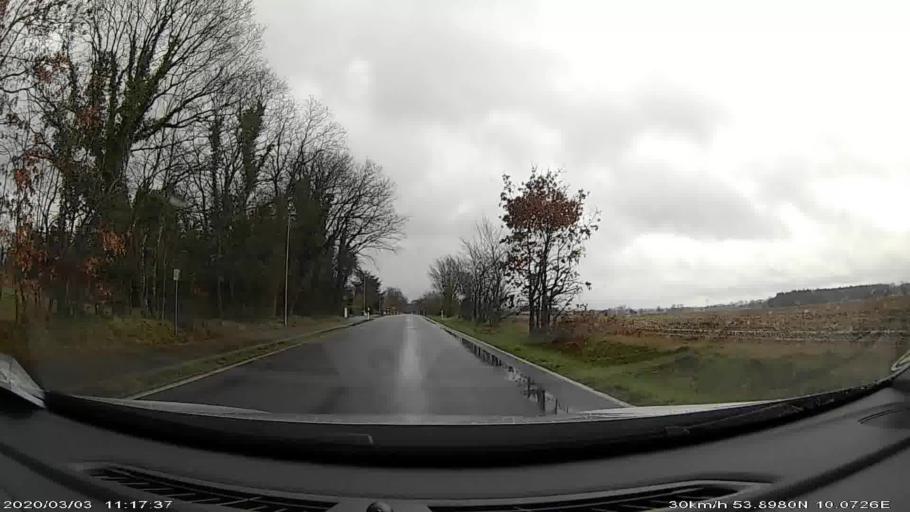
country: DE
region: Schleswig-Holstein
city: Hartenholm
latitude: 53.8965
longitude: 10.0757
